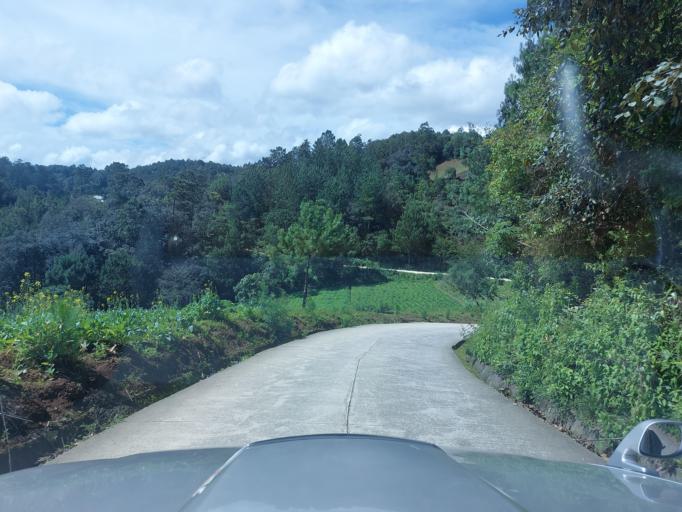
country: GT
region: Chimaltenango
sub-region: Municipio de San Juan Comalapa
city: Comalapa
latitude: 14.7557
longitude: -90.8727
